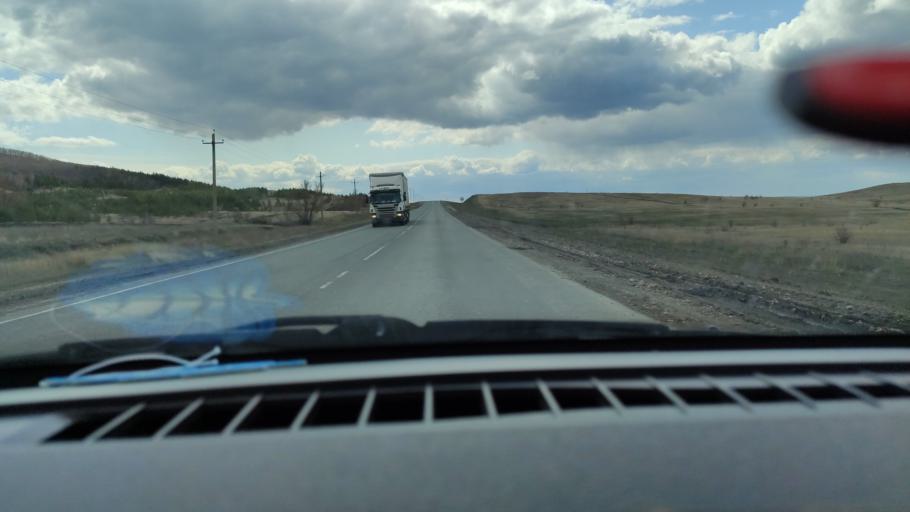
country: RU
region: Saratov
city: Alekseyevka
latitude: 52.3010
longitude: 47.9271
